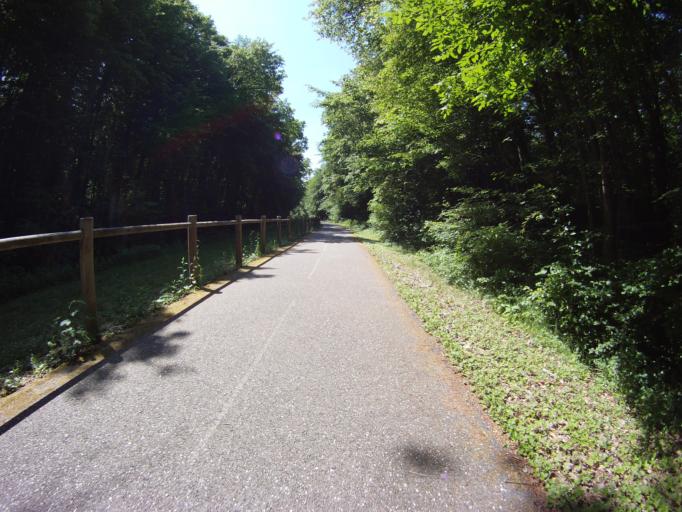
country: FR
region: Lorraine
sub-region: Departement de Meurthe-et-Moselle
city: Champenoux
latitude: 48.7523
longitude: 6.3253
